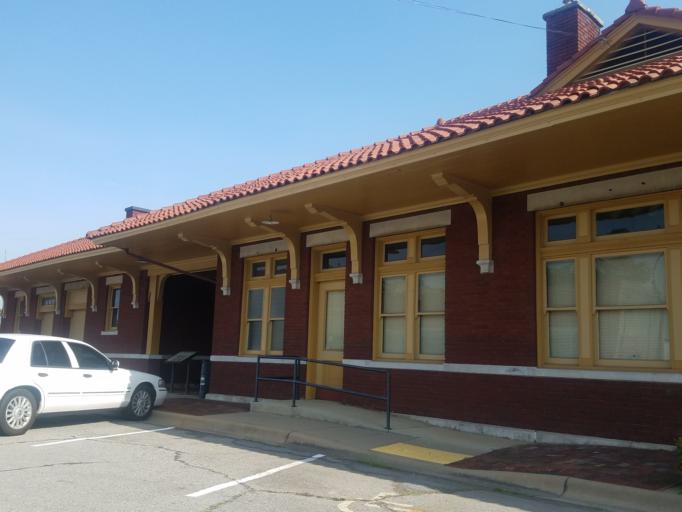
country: US
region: Arkansas
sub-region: Conway County
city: Morrilton
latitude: 35.1522
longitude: -92.7442
